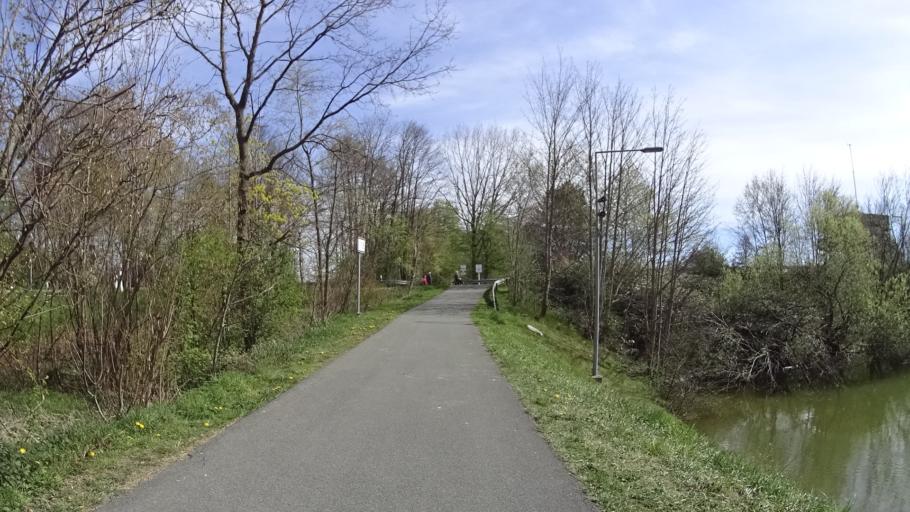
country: DE
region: North Rhine-Westphalia
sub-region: Regierungsbezirk Munster
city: Dreierwalde
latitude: 52.3069
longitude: 7.4747
